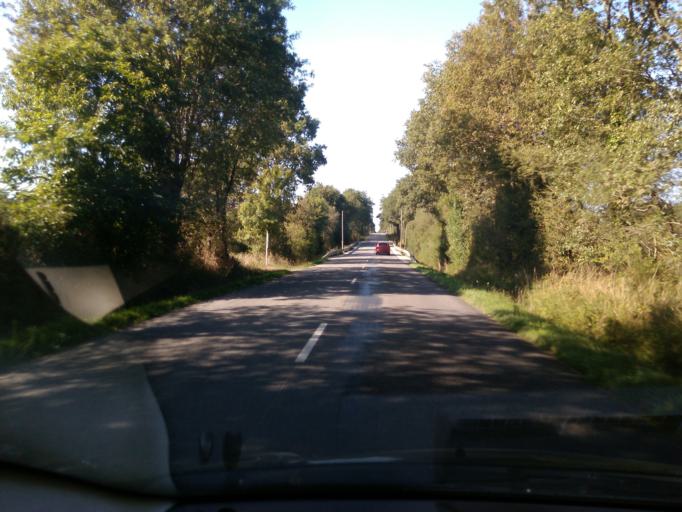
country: FR
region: Pays de la Loire
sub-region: Departement de la Loire-Atlantique
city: Quilly
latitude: 47.4379
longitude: -1.9257
